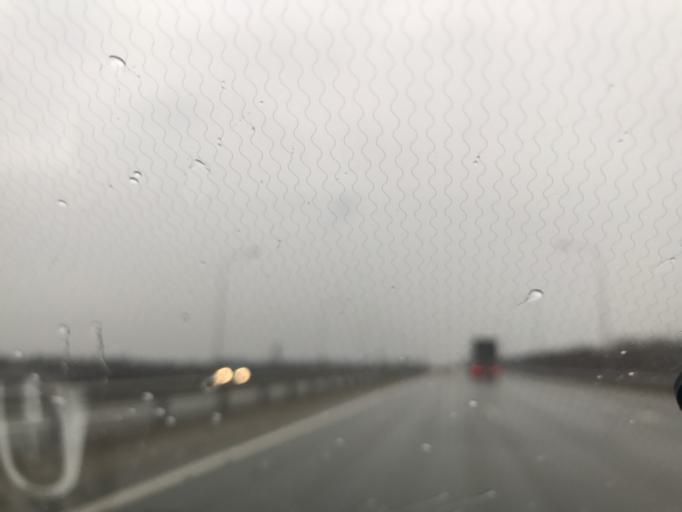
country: RU
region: Krasnodarskiy
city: Krylovskaya
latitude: 46.3036
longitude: 39.8124
